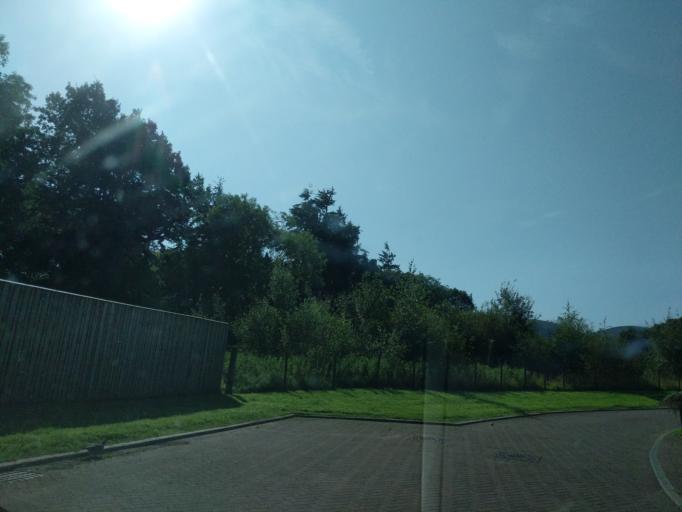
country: GB
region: Scotland
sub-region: The Scottish Borders
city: Peebles
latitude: 55.6409
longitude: -3.1858
